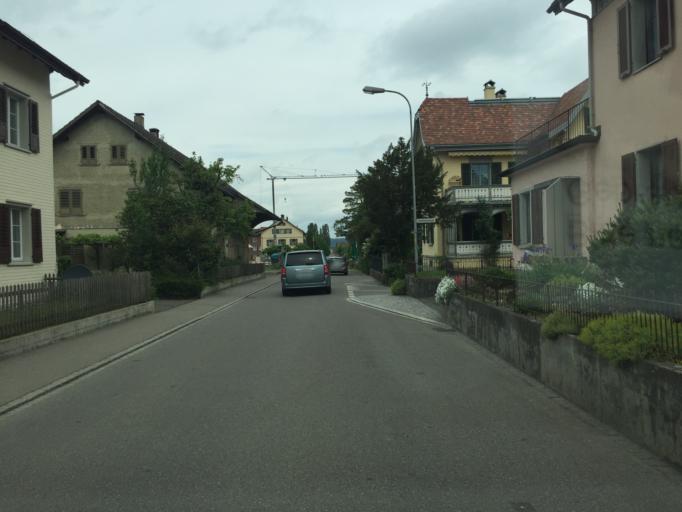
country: CH
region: Thurgau
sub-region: Kreuzlingen District
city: Ermatingen
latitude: 47.6708
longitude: 9.0843
